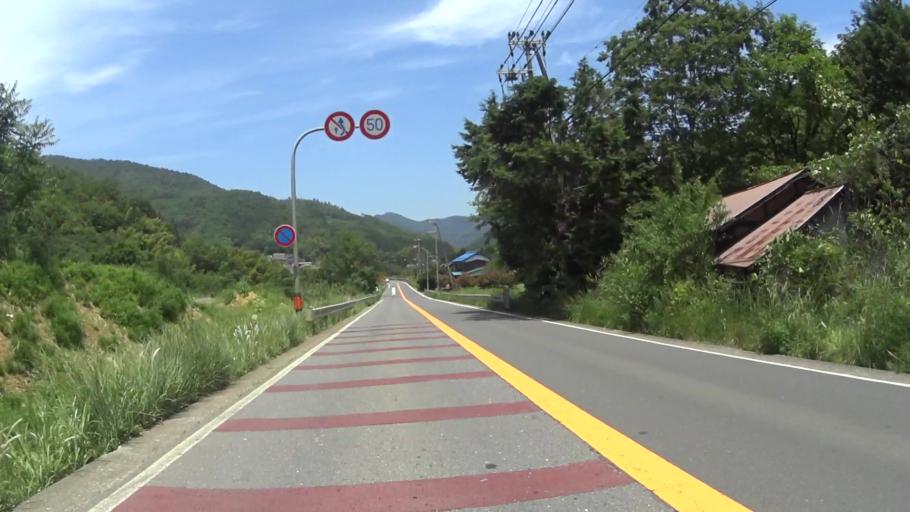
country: JP
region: Kyoto
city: Ayabe
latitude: 35.2045
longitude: 135.2826
